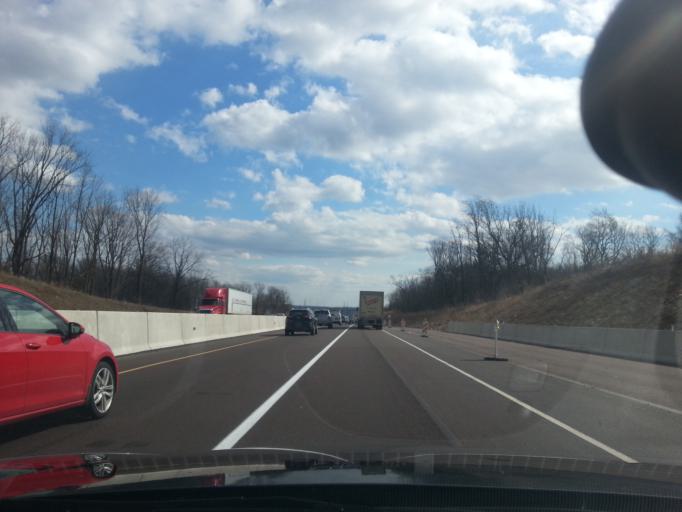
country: US
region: Pennsylvania
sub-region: Montgomery County
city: North Wales
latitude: 40.1885
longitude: -75.3136
